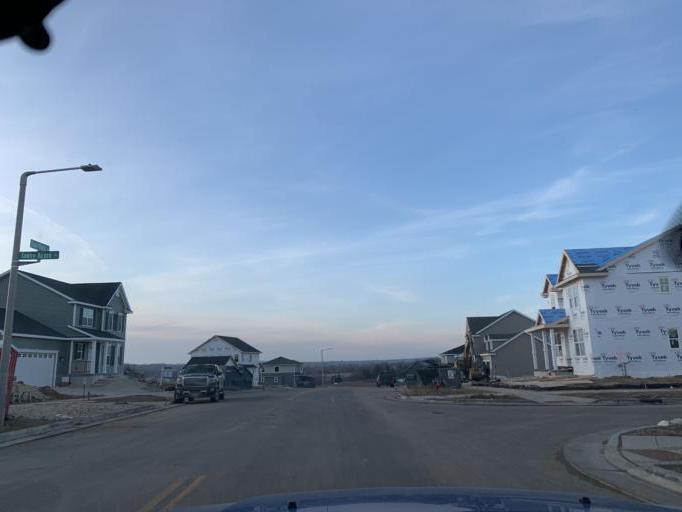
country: US
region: Wisconsin
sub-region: Dane County
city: Verona
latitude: 43.0470
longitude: -89.5581
